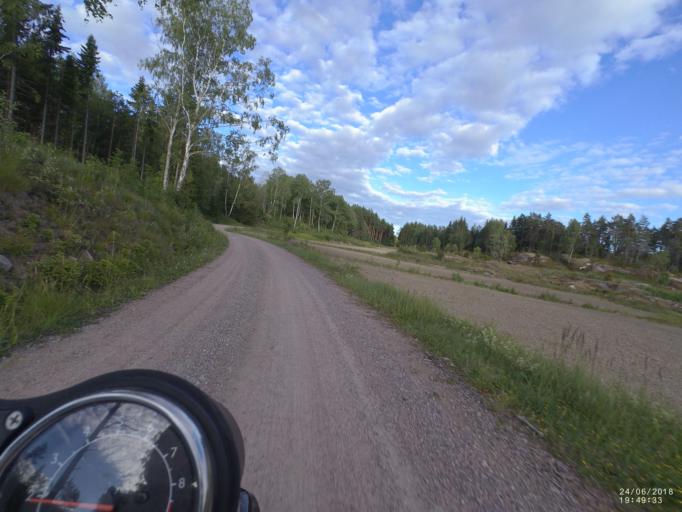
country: SE
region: Soedermanland
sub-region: Oxelosunds Kommun
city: Oxelosund
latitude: 58.7797
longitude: 17.1405
